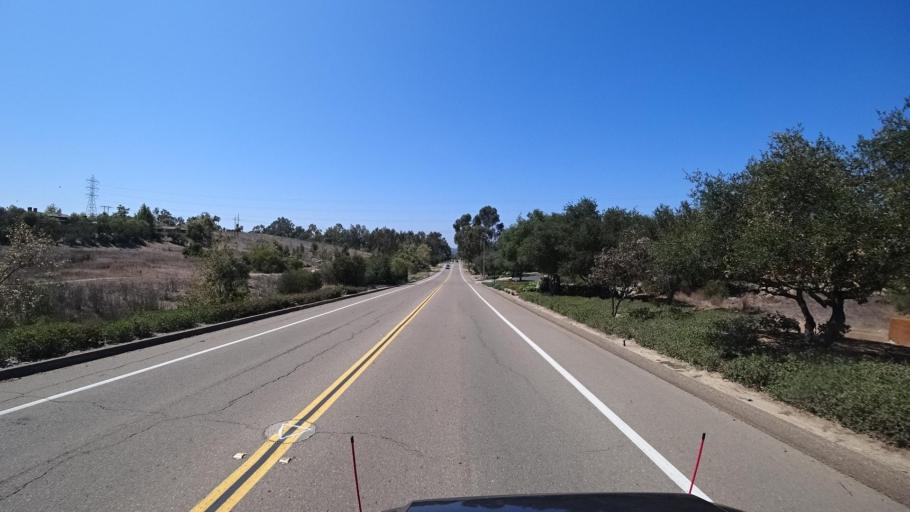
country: US
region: California
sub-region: San Diego County
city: Fairbanks Ranch
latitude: 33.0046
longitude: -117.1669
